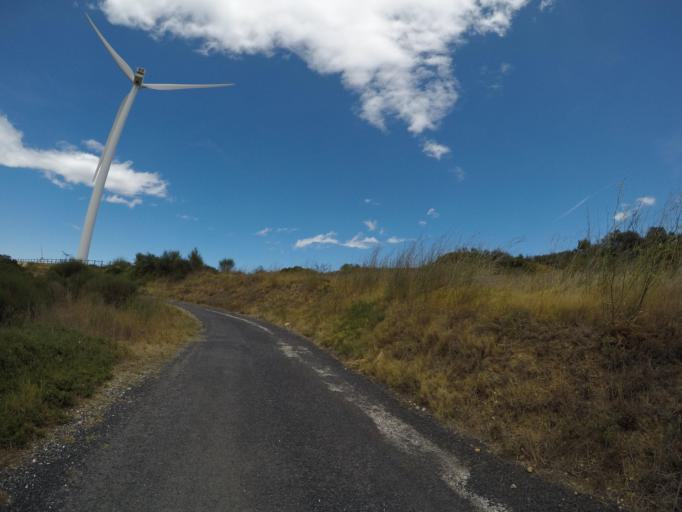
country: FR
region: Languedoc-Roussillon
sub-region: Departement des Pyrenees-Orientales
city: Pezilla-la-Riviere
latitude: 42.7178
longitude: 2.7617
